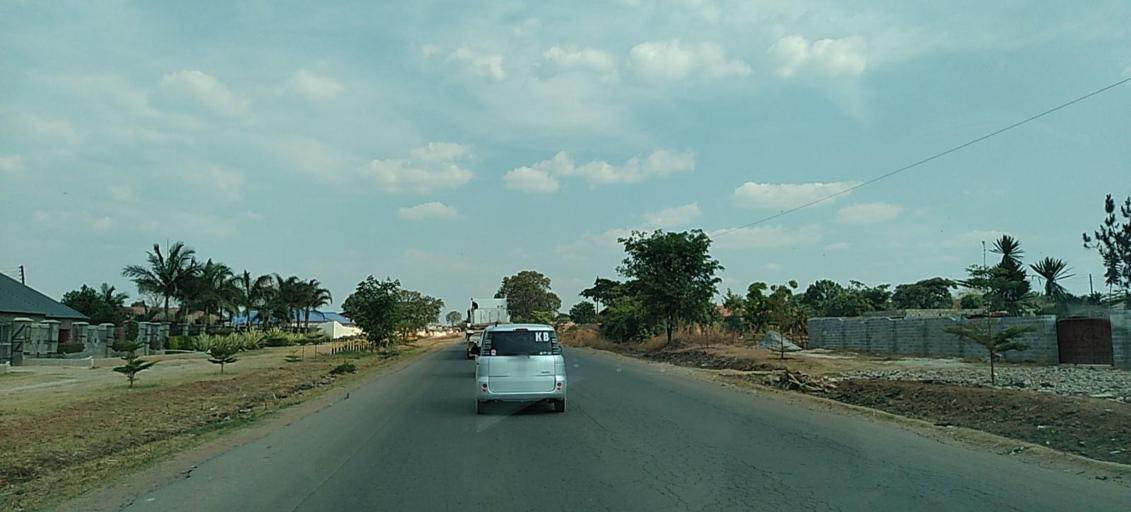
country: ZM
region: Copperbelt
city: Chililabombwe
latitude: -12.3603
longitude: 27.8490
